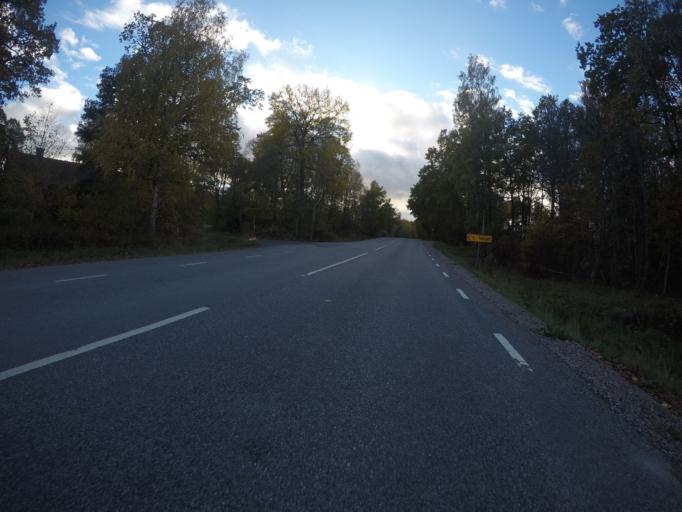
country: SE
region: Vaestmanland
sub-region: Arboga Kommun
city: Tyringe
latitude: 59.3133
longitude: 15.9717
